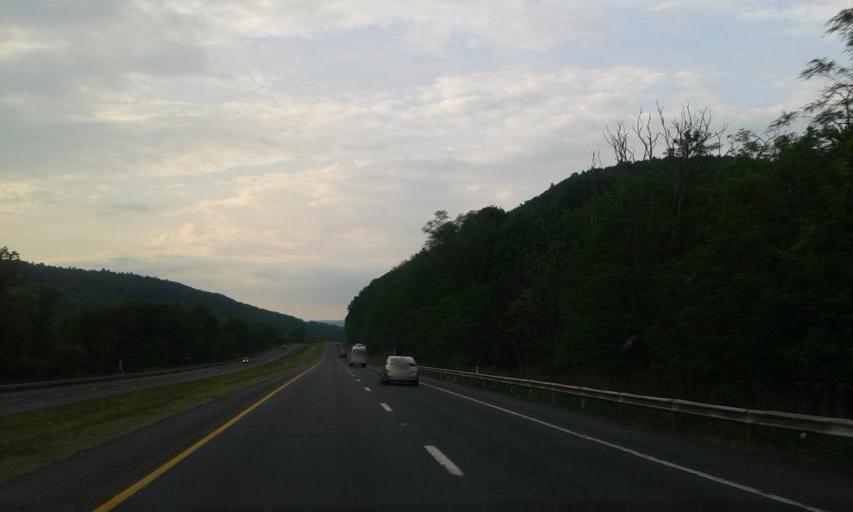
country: US
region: Pennsylvania
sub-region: Susquehanna County
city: Hallstead
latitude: 41.9048
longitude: -75.7301
